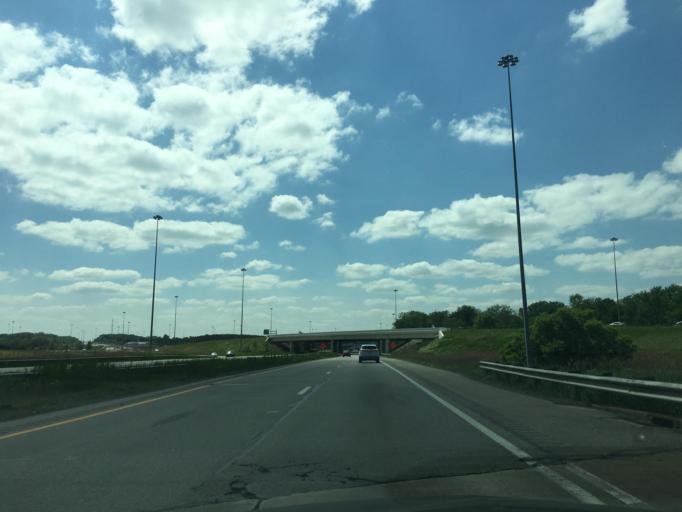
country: US
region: Ohio
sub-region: Medina County
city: Seville
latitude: 41.0313
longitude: -81.8840
